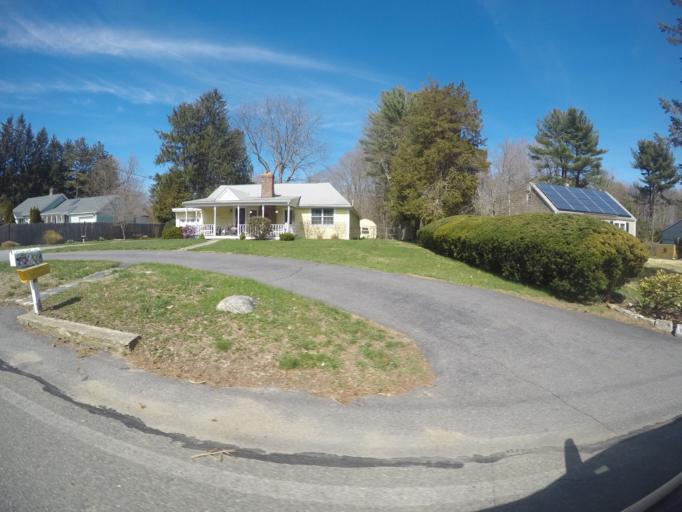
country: US
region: Massachusetts
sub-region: Bristol County
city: Easton
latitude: 42.0248
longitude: -71.0818
